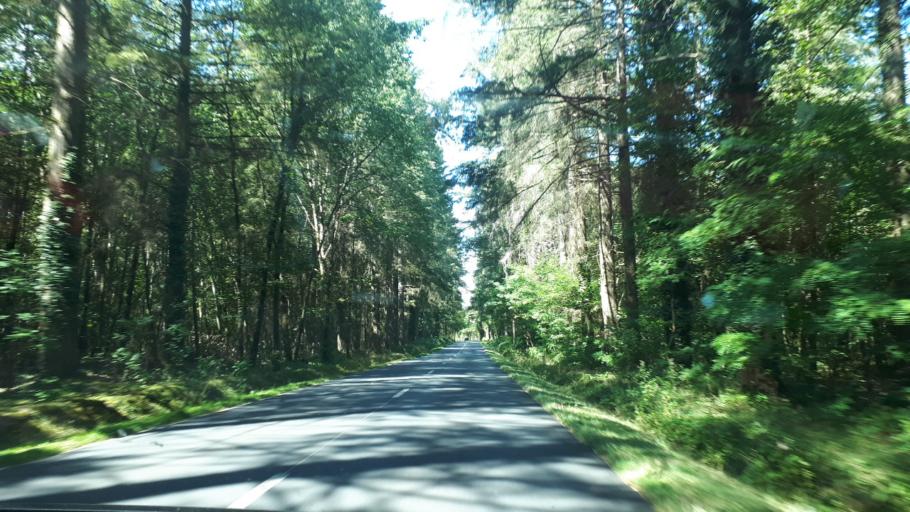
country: FR
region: Centre
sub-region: Departement du Loir-et-Cher
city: Chaumont-sur-Tharonne
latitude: 47.5761
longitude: 1.9305
